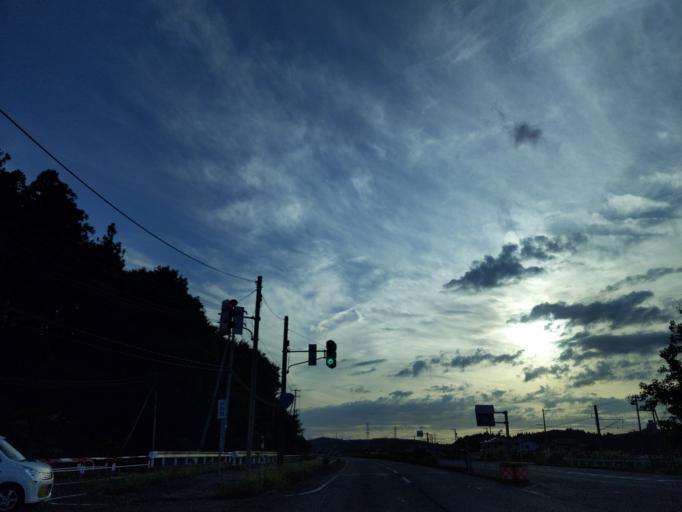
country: JP
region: Niigata
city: Kashiwazaki
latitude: 37.4525
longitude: 138.6512
